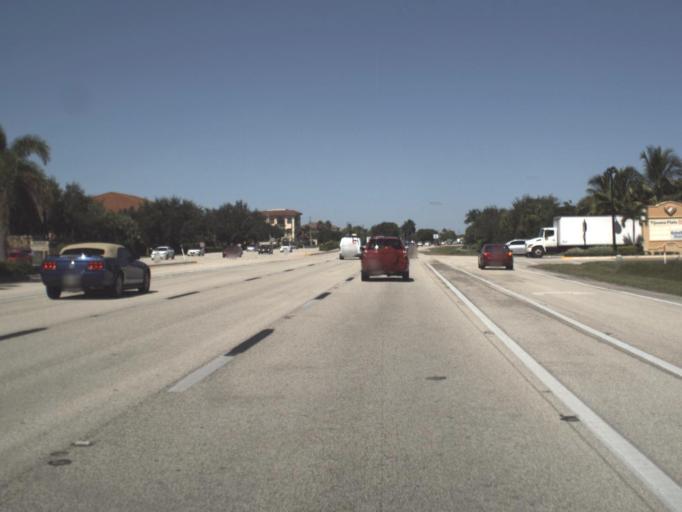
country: US
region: Florida
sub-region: Lee County
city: Estero
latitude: 26.3917
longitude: -81.8098
